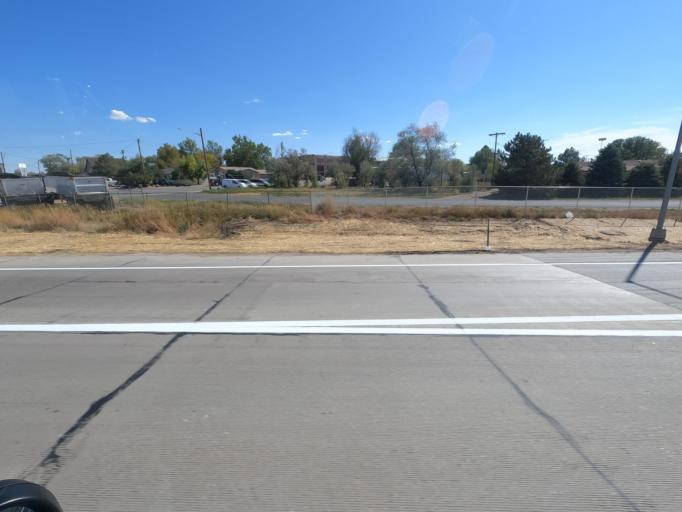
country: US
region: Colorado
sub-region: Weld County
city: Hudson
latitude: 40.0761
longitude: -104.6446
